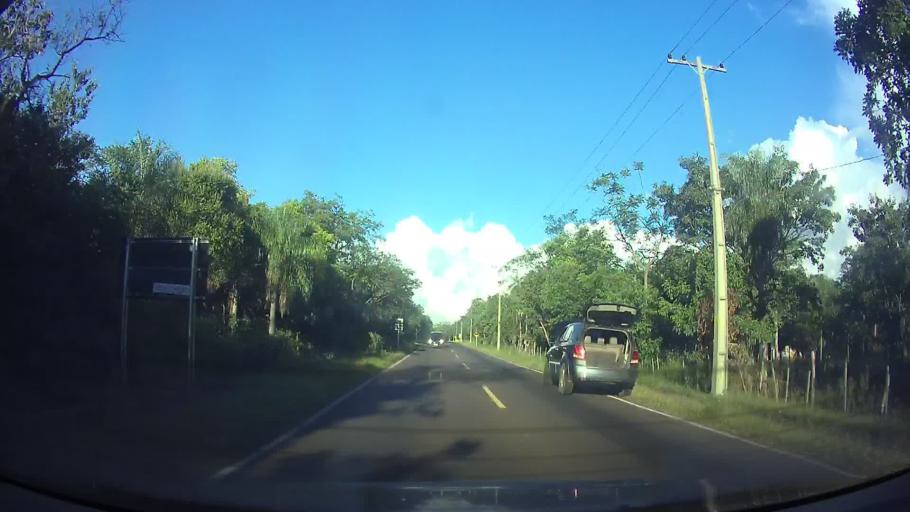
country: PY
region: Cordillera
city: Emboscada
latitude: -25.2053
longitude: -57.3457
